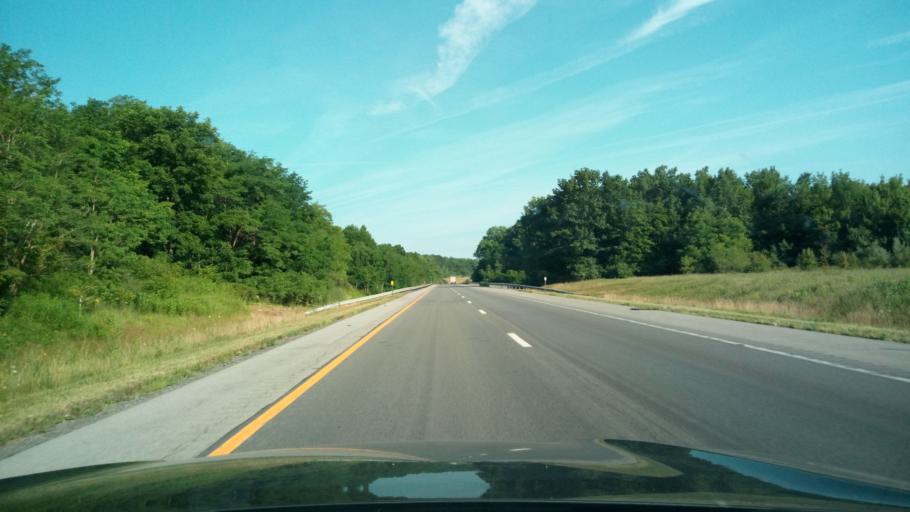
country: US
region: New York
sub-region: Livingston County
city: Dansville
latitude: 42.6079
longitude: -77.7594
